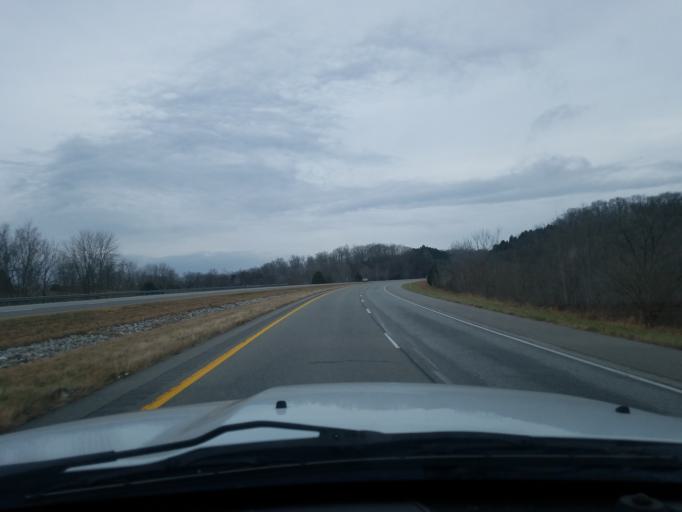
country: US
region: Indiana
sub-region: Harrison County
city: Corydon
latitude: 38.2347
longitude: -86.2329
